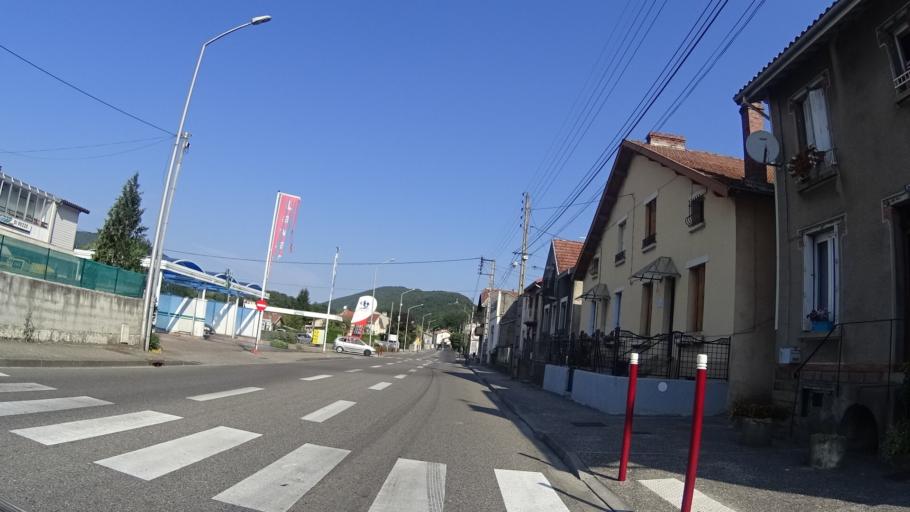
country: FR
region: Midi-Pyrenees
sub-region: Departement de l'Ariege
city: Lavelanet
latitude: 42.9280
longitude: 1.8591
